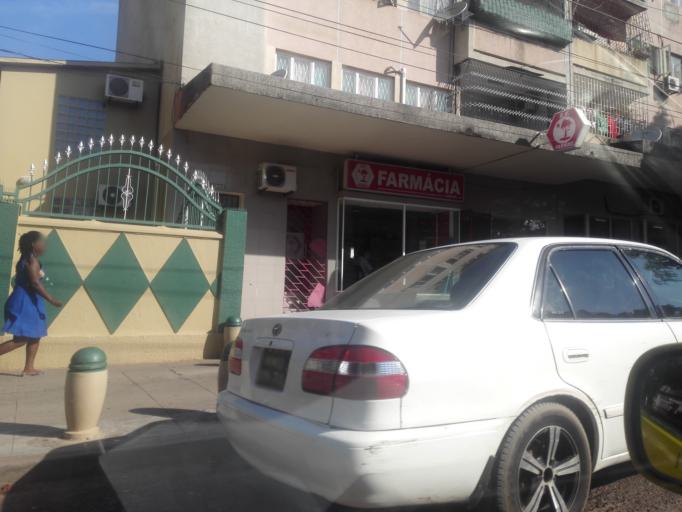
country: MZ
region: Maputo City
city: Maputo
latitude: -25.9632
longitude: 32.5814
